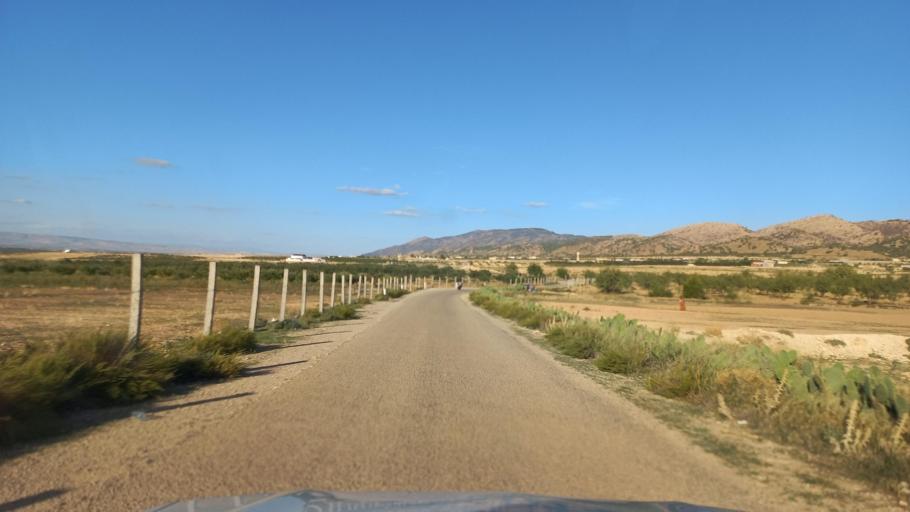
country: TN
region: Al Qasrayn
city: Sbiba
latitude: 35.3574
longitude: 9.1398
